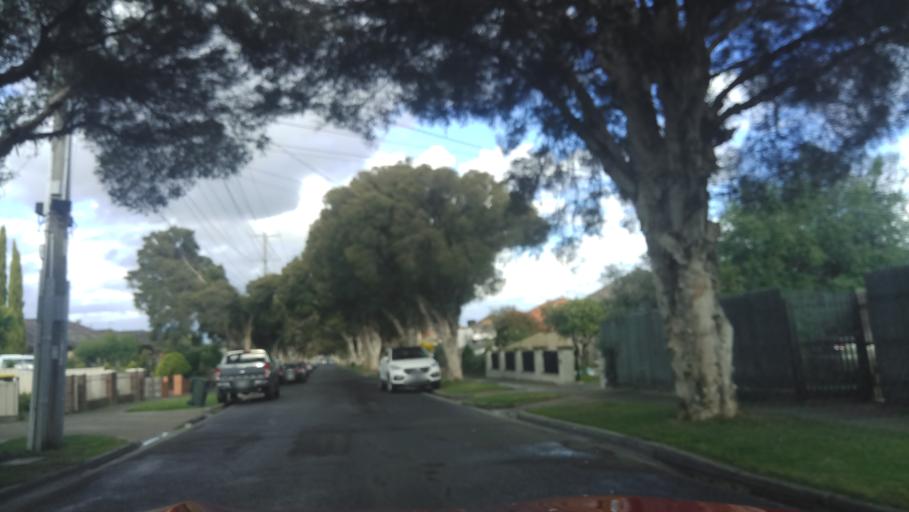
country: AU
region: Victoria
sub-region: Hobsons Bay
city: Altona North
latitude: -37.8264
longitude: 144.8513
